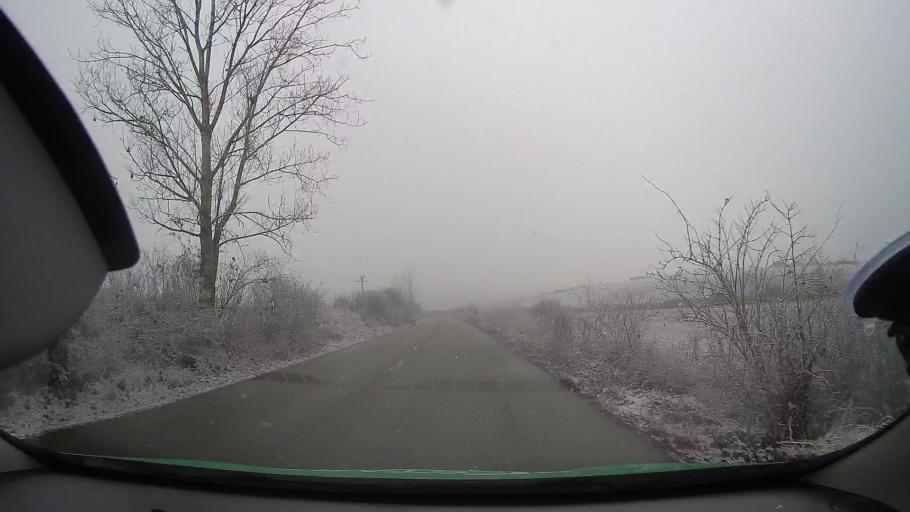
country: RO
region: Alba
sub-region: Comuna Noslac
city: Noslac
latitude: 46.3769
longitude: 23.9080
